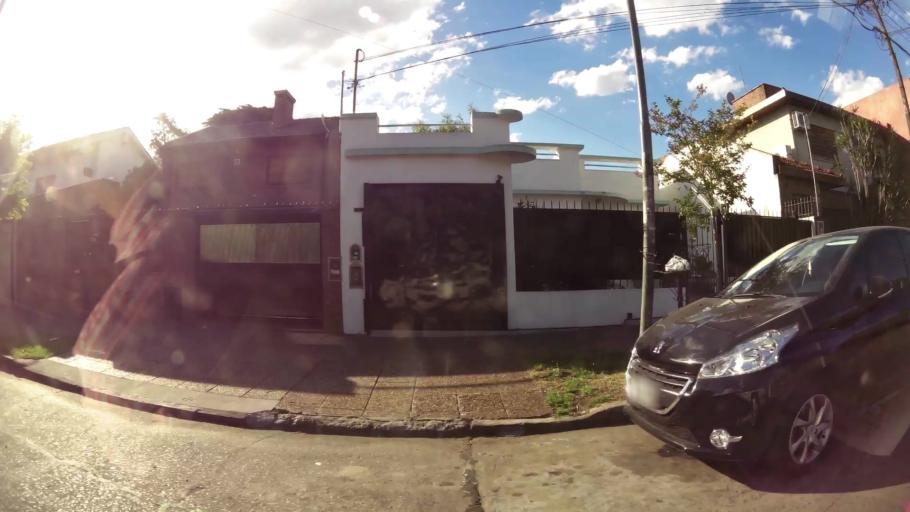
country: AR
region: Buenos Aires
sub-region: Partido de General San Martin
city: General San Martin
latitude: -34.5406
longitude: -58.5660
